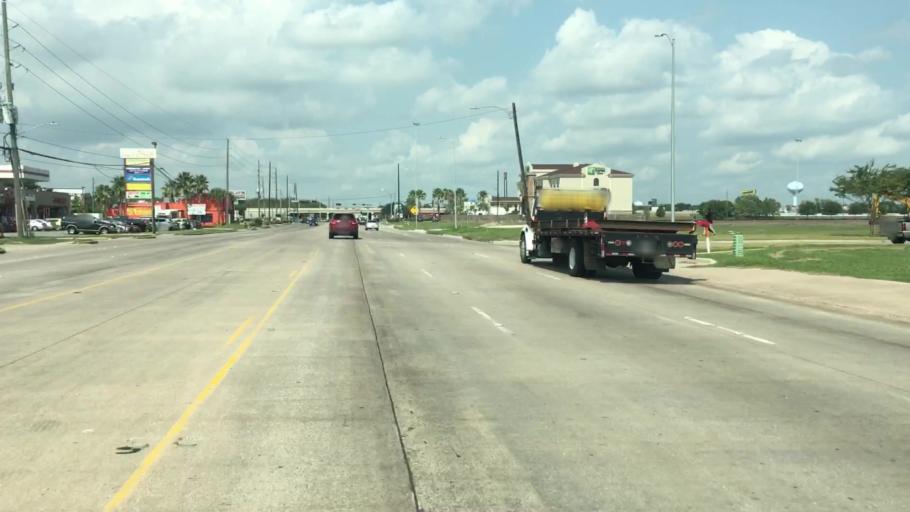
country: US
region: Texas
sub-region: Harris County
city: Aldine
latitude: 29.9318
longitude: -95.4069
